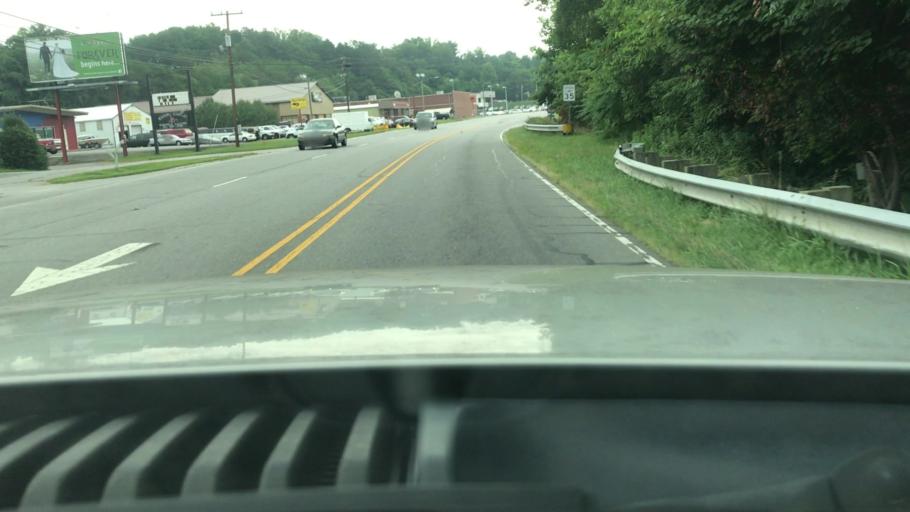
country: US
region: North Carolina
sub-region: Wilkes County
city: Wilkesboro
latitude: 36.1547
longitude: -81.1714
